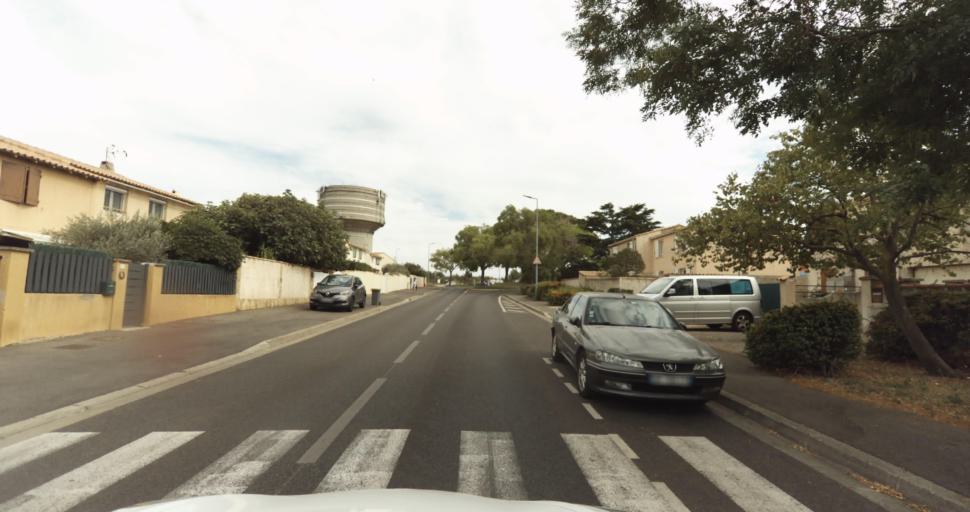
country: FR
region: Provence-Alpes-Cote d'Azur
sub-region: Departement des Bouches-du-Rhone
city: Miramas
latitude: 43.5735
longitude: 5.0037
